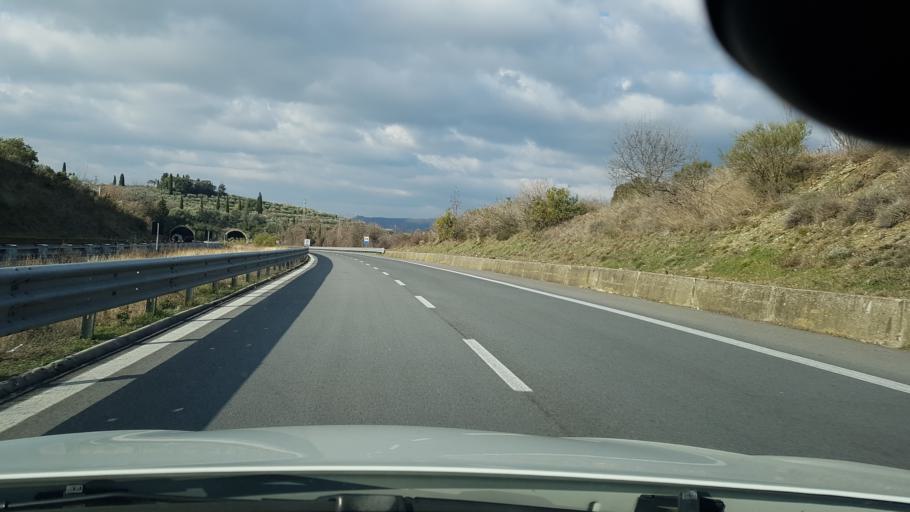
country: IT
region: Umbria
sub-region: Provincia di Perugia
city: Passignano sul Trasimeno
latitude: 43.1972
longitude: 12.1286
